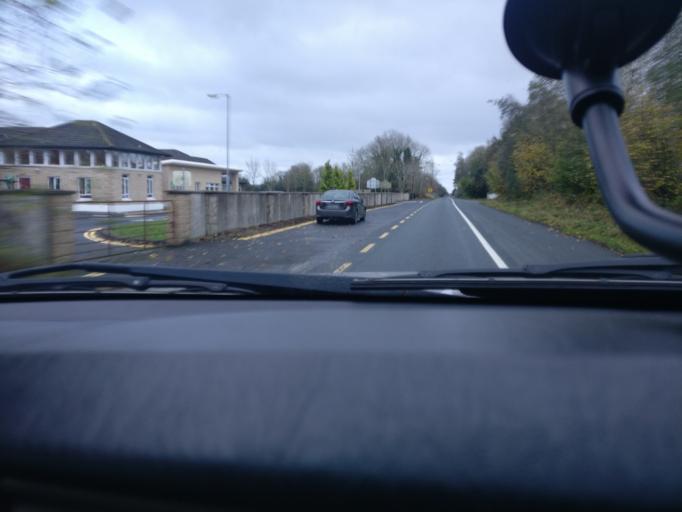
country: IE
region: Leinster
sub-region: Kildare
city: Kilcock
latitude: 53.4088
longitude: -6.6995
